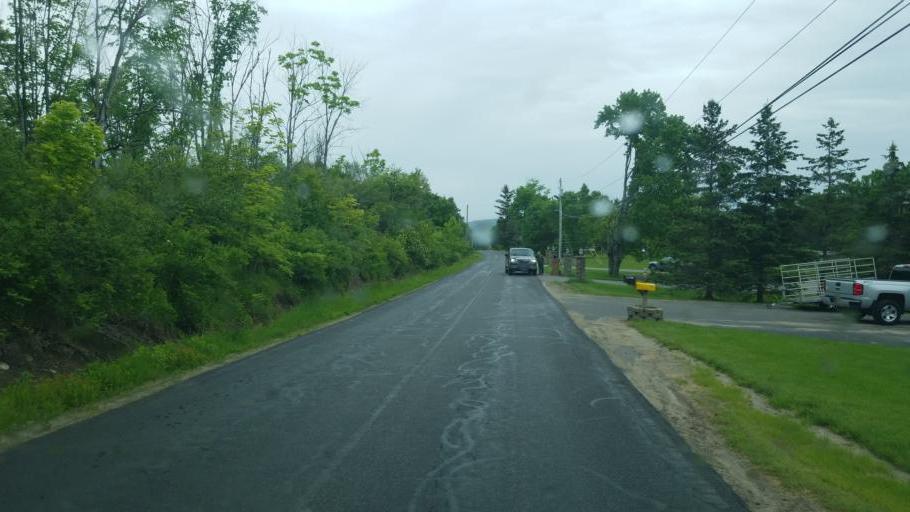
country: US
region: New York
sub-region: Herkimer County
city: Mohawk
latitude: 43.0441
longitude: -75.0151
